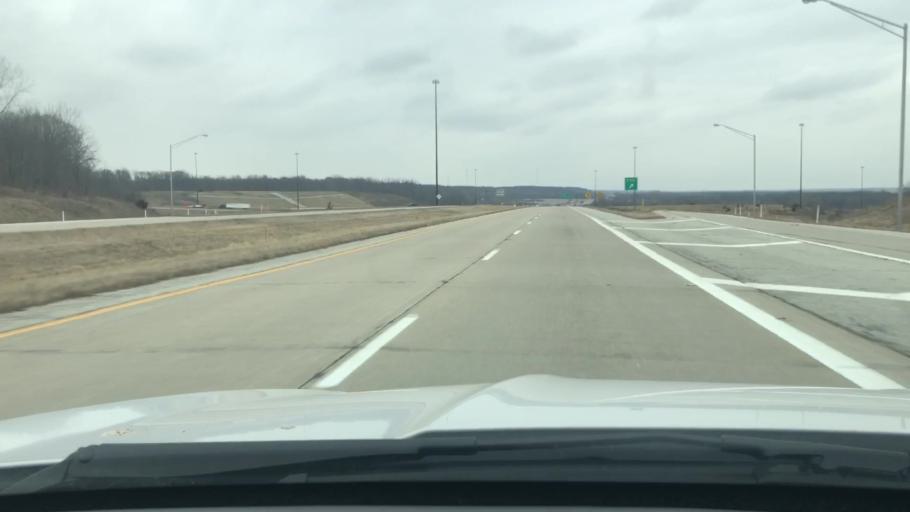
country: US
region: Indiana
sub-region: Miami County
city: Peru
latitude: 40.7715
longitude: -86.1347
